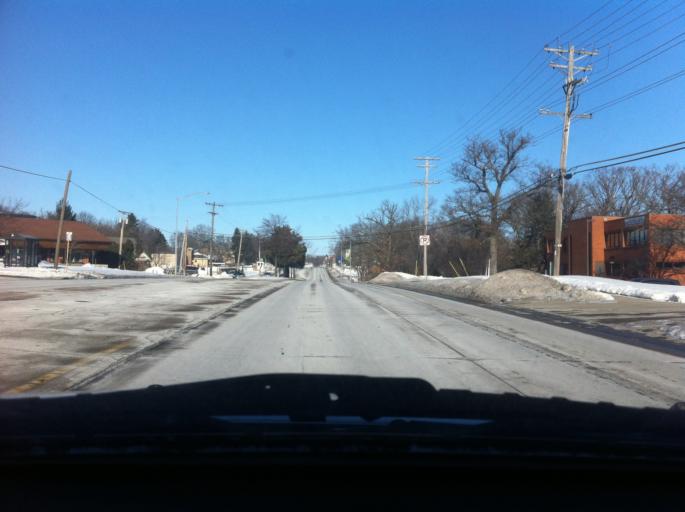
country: US
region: Wisconsin
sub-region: Dane County
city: Middleton
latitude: 43.0920
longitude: -89.4893
